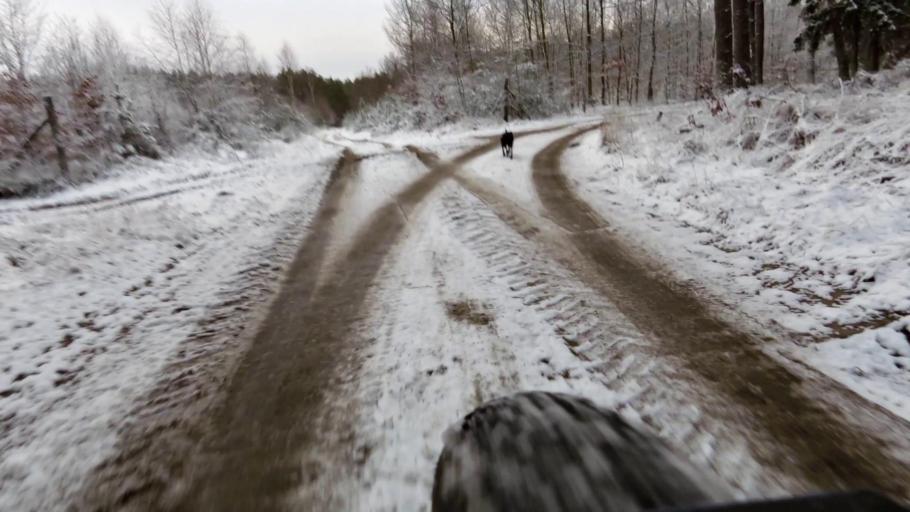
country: PL
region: West Pomeranian Voivodeship
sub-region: Powiat walecki
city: Miroslawiec
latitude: 53.3772
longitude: 16.1456
